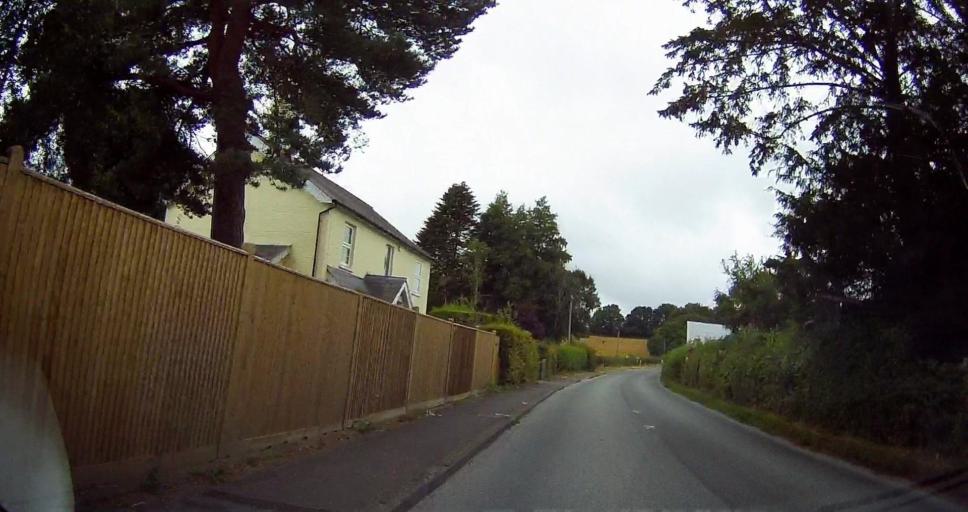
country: GB
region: England
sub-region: East Sussex
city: Wadhurst
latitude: 51.0729
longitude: 0.3456
